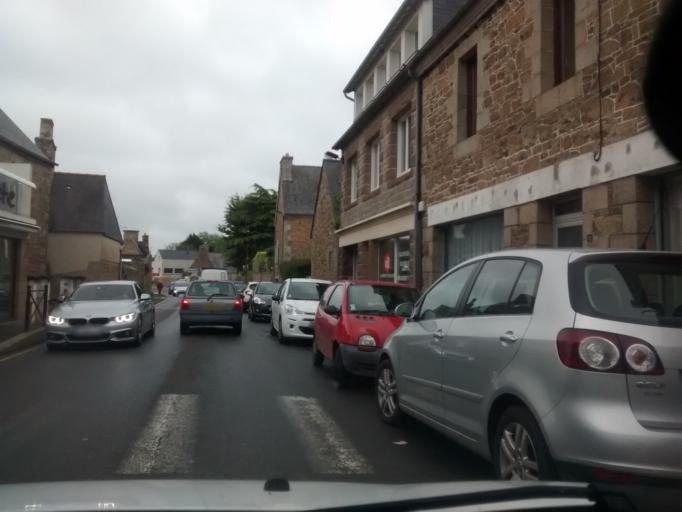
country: FR
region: Brittany
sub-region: Departement des Cotes-d'Armor
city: Penvenan
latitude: 48.8108
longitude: -3.2956
